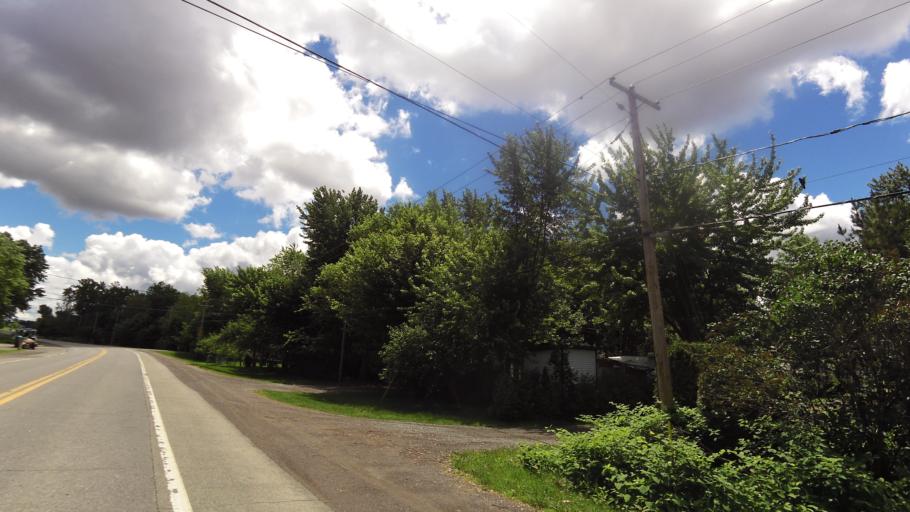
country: CA
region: Quebec
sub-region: Monteregie
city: Rigaud
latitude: 45.5328
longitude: -74.2507
